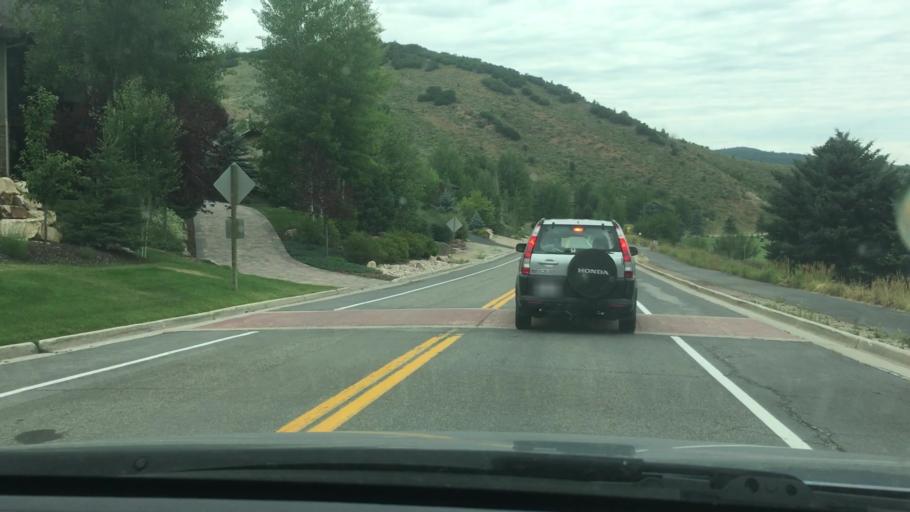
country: US
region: Utah
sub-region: Summit County
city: Summit Park
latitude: 40.7635
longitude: -111.5801
